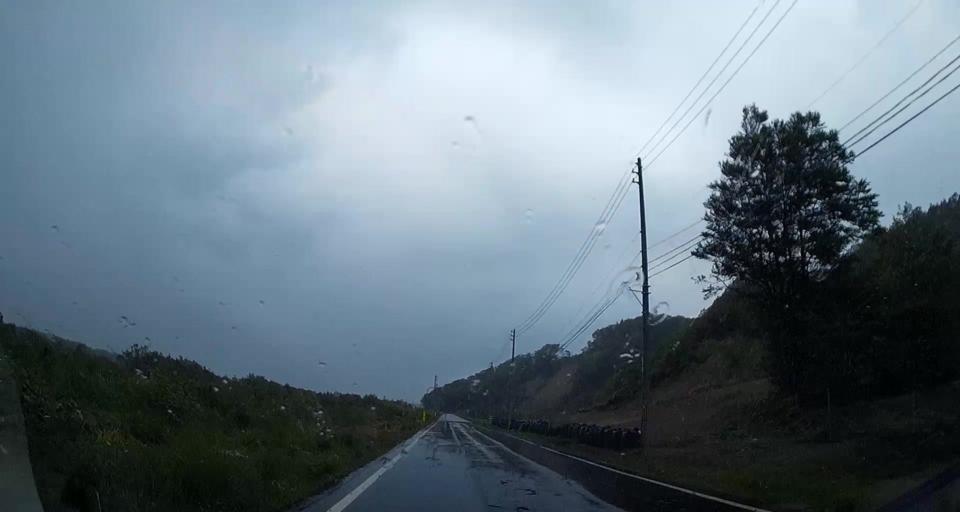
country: JP
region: Hokkaido
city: Chitose
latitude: 42.7422
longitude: 141.9051
